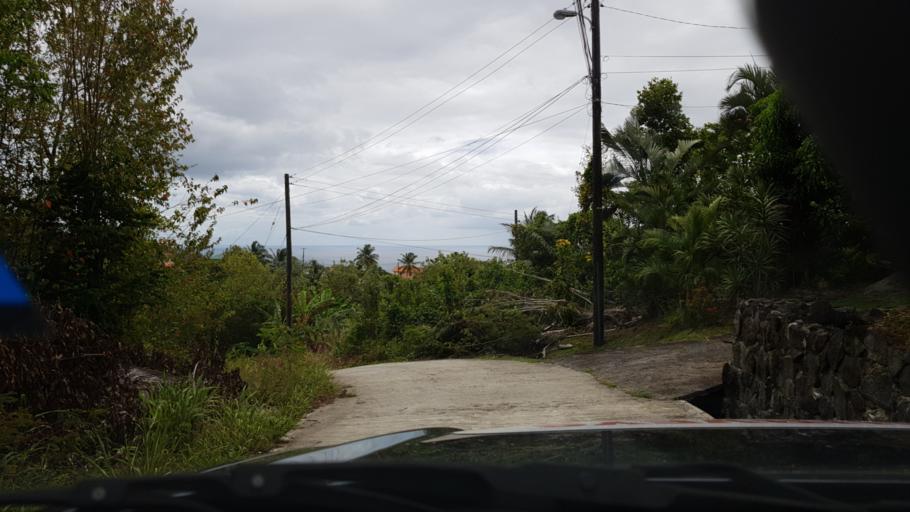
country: LC
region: Anse-la-Raye
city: Anse La Raye
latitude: 13.9467
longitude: -61.0348
